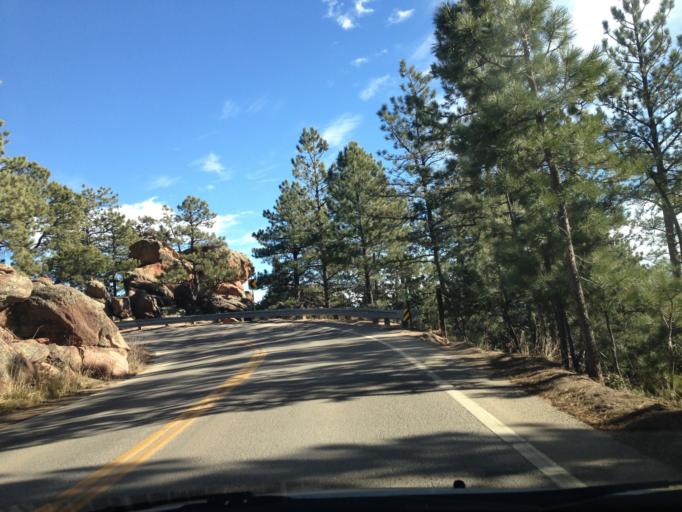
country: US
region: Colorado
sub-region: Boulder County
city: Boulder
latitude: 40.0026
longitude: -105.2956
